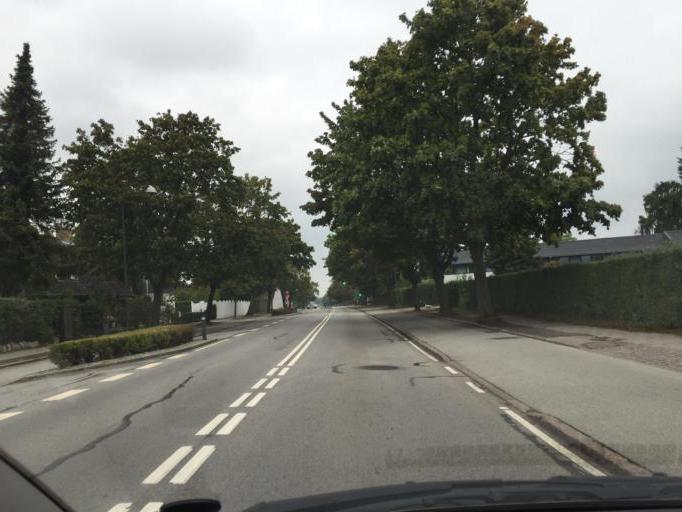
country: DK
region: Capital Region
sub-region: Herlev Kommune
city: Herlev
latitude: 55.7359
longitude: 12.4333
